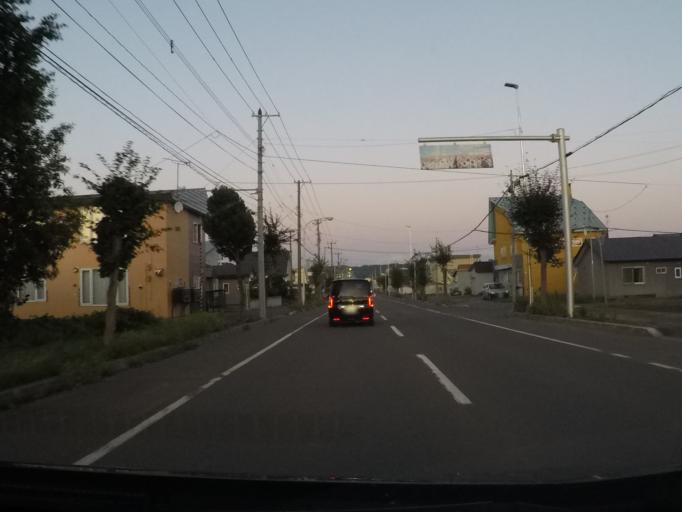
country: JP
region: Hokkaido
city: Nayoro
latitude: 44.3464
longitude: 142.4464
